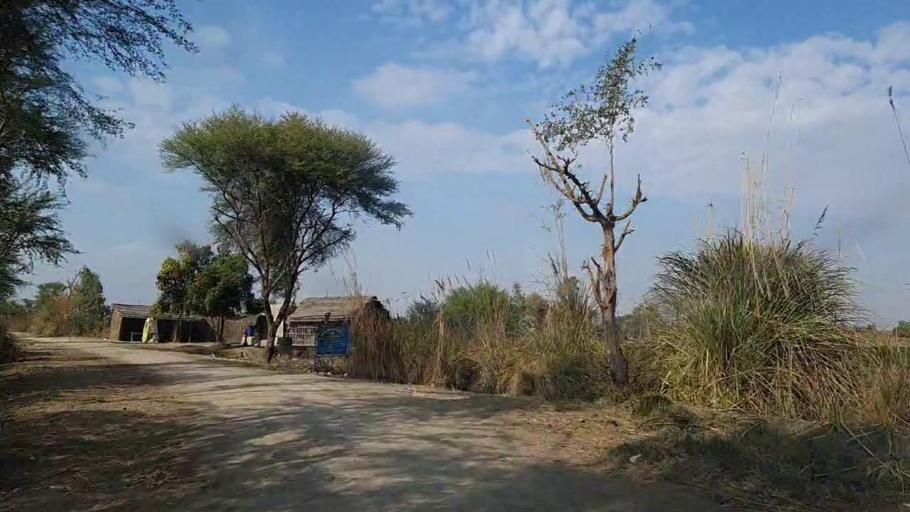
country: PK
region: Sindh
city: Sanghar
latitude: 26.2584
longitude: 69.0095
